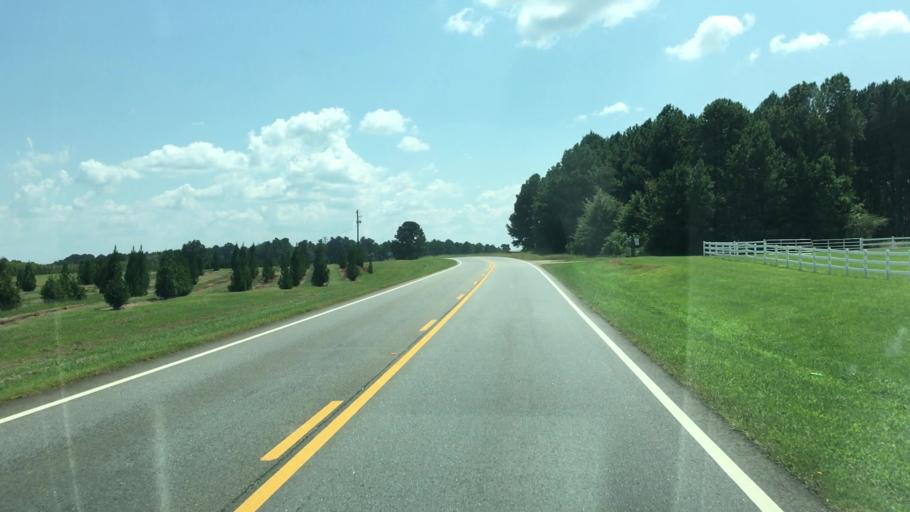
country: US
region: Georgia
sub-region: Oconee County
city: Watkinsville
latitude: 33.7564
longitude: -83.4353
